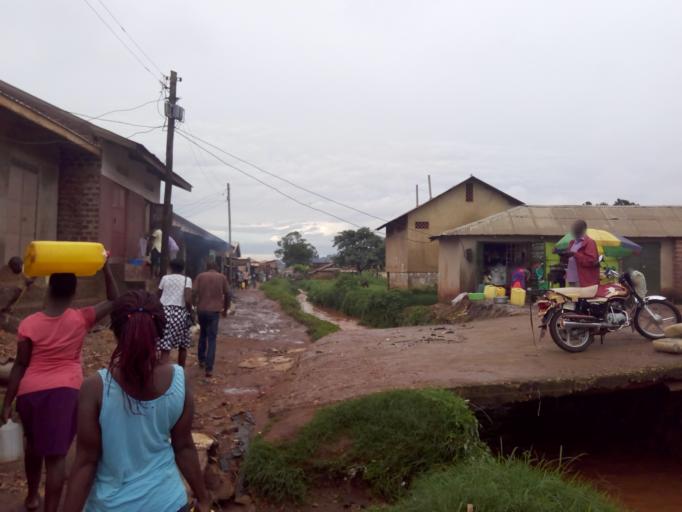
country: UG
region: Central Region
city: Kampala Central Division
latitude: 0.3369
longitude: 32.5590
